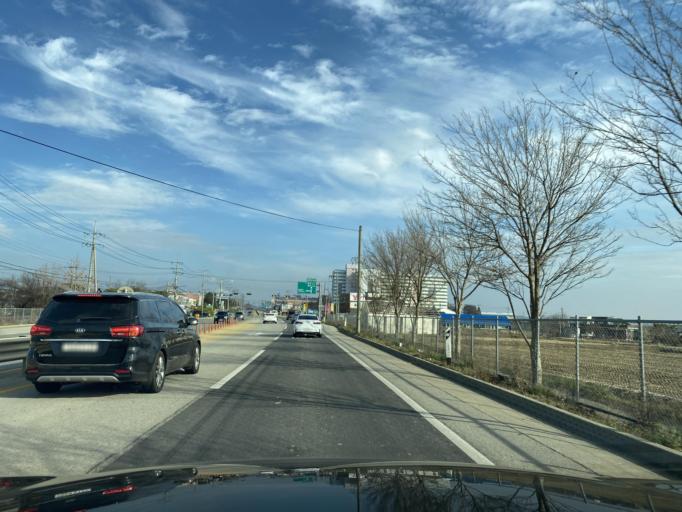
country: KR
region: Chungcheongnam-do
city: Yesan
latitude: 36.6860
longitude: 126.7723
